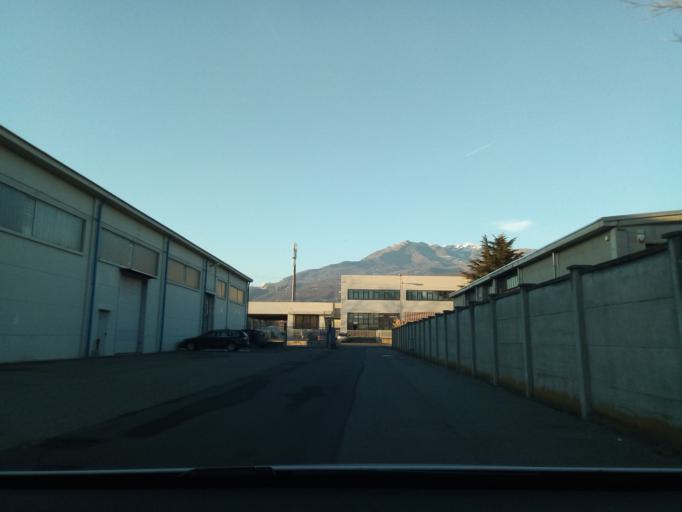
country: IT
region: Piedmont
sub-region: Provincia di Torino
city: Burolo
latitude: 45.4735
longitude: 7.9208
